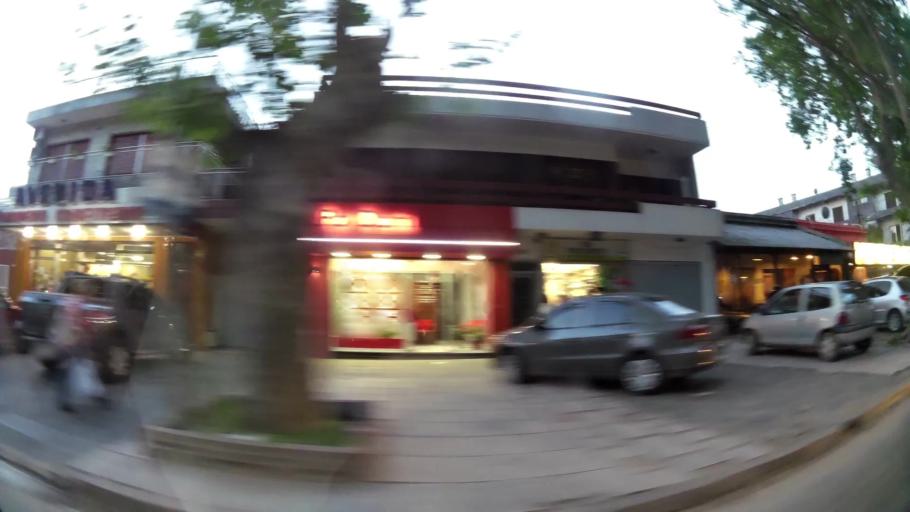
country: AR
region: Buenos Aires
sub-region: Partido de Quilmes
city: Quilmes
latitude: -34.8084
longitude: -58.2784
